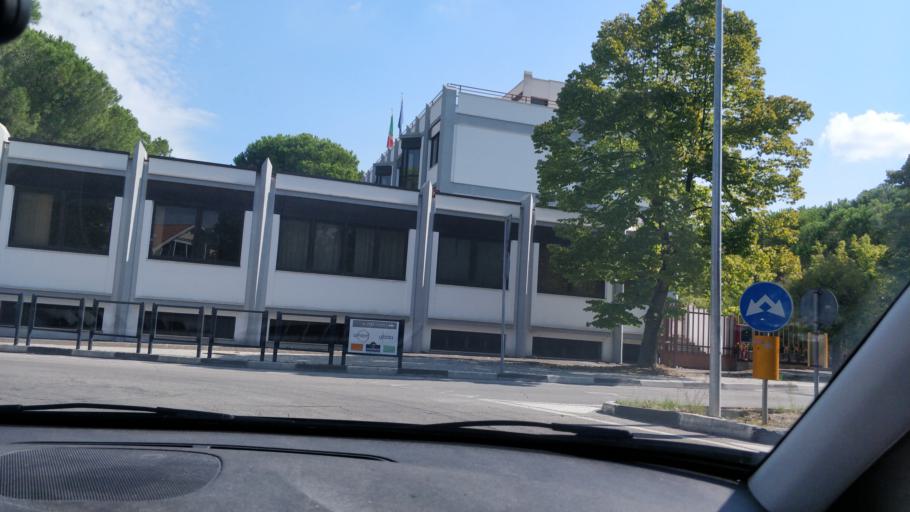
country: IT
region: Abruzzo
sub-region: Provincia di Chieti
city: Chieti
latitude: 42.3753
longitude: 14.1449
